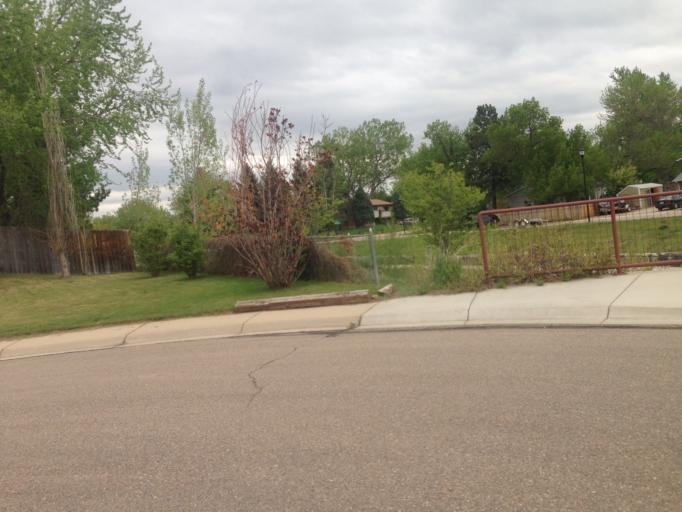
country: US
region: Colorado
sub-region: Boulder County
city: Longmont
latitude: 40.1385
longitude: -105.1170
